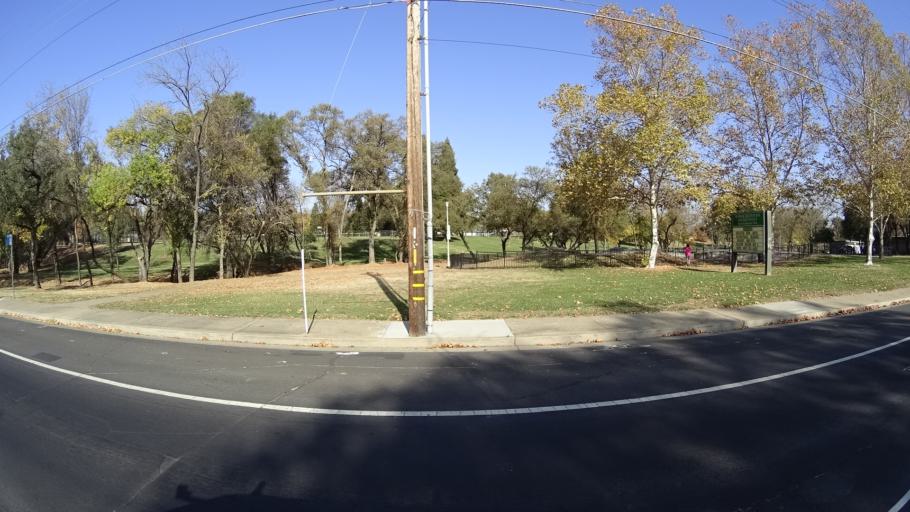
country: US
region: California
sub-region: Sacramento County
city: Citrus Heights
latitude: 38.7075
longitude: -121.2953
